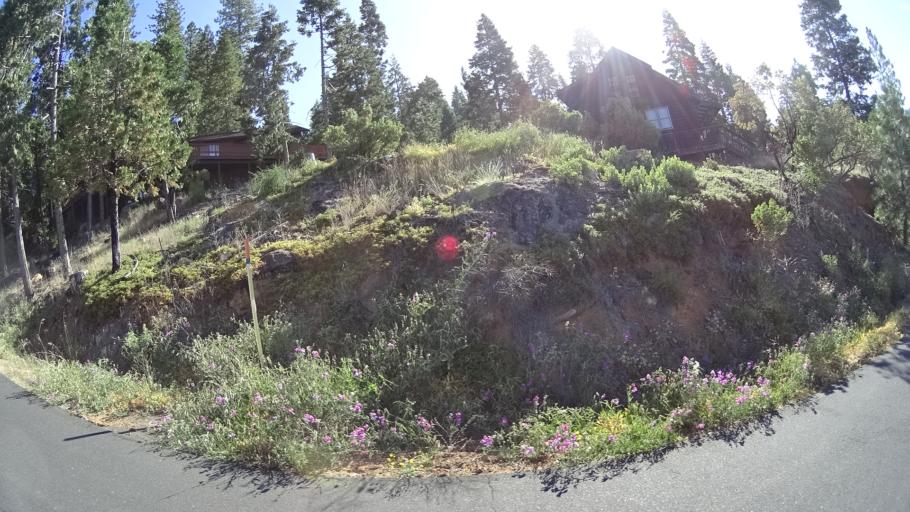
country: US
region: California
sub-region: Calaveras County
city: Arnold
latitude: 38.2624
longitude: -120.3277
